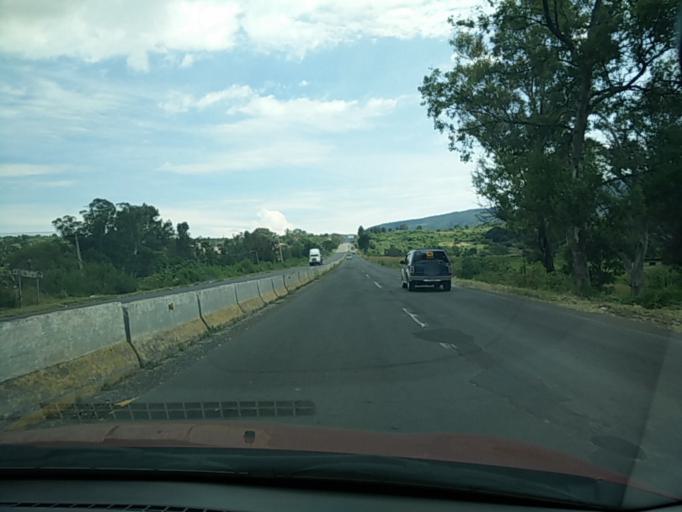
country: MX
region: Jalisco
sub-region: Ixtlahuacan de los Membrillos
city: Los Cedros
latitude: 20.3824
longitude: -103.2188
